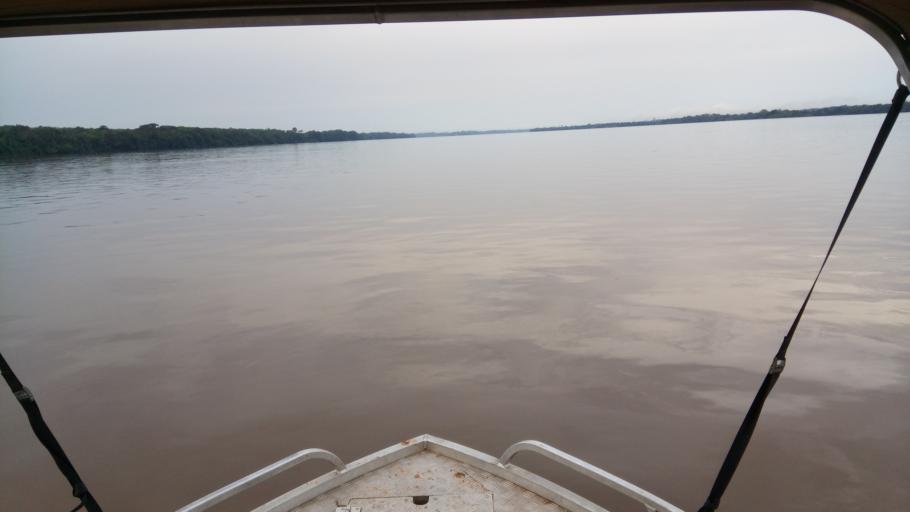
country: CD
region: Eastern Province
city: Kisangani
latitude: 0.5738
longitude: 24.8370
